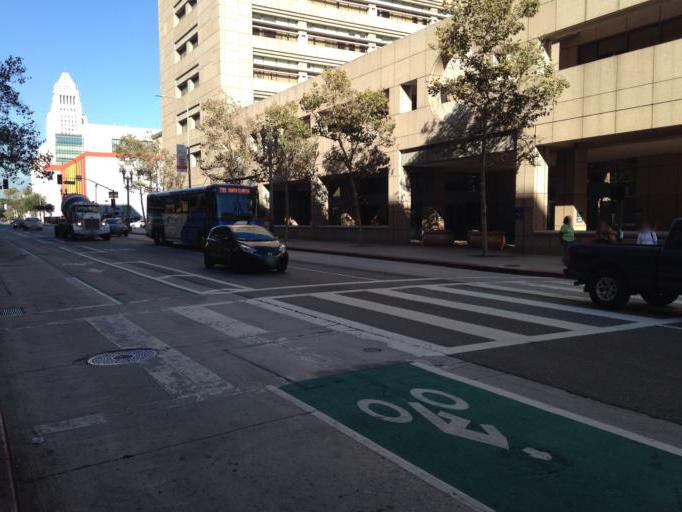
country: US
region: California
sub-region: Los Angeles County
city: Los Angeles
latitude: 34.0495
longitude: -118.2472
